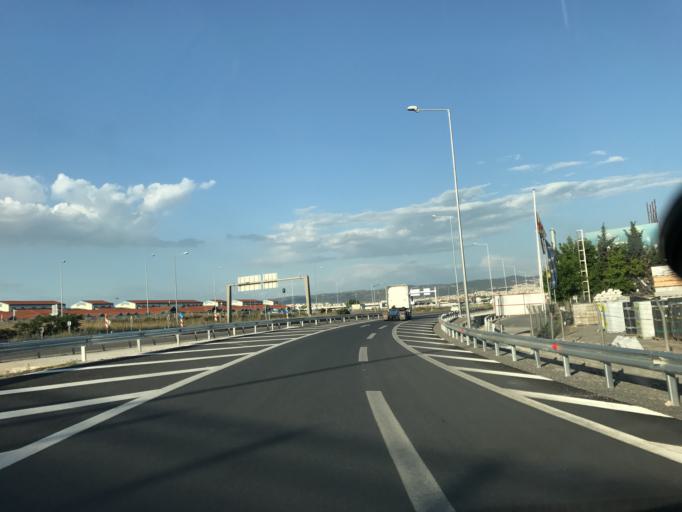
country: GR
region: Central Macedonia
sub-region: Nomos Thessalonikis
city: Menemeni
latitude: 40.6551
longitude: 22.8827
